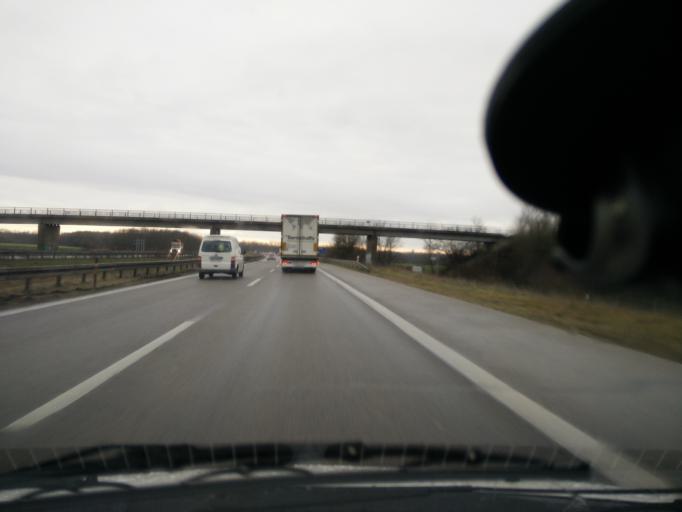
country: DE
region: Bavaria
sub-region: Upper Bavaria
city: Oberschleissheim
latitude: 48.2461
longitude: 11.5332
